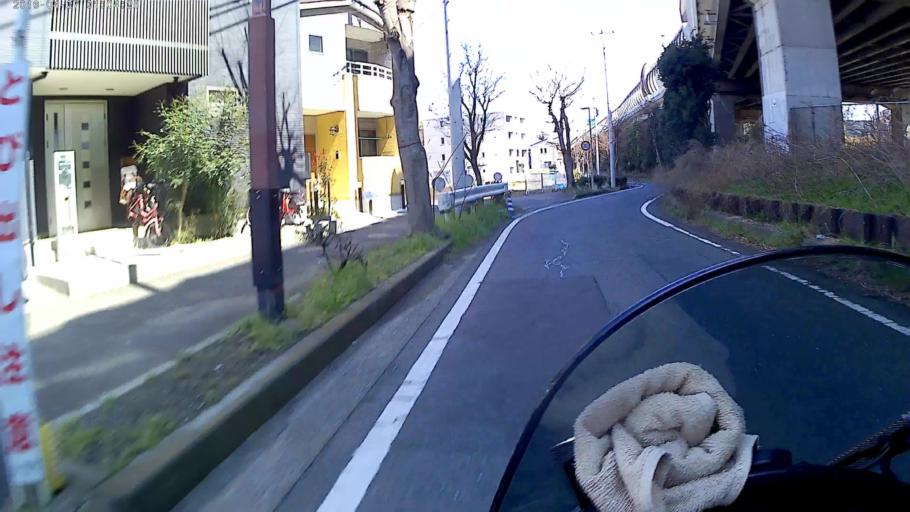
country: JP
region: Kanagawa
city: Fujisawa
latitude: 35.3473
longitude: 139.4377
